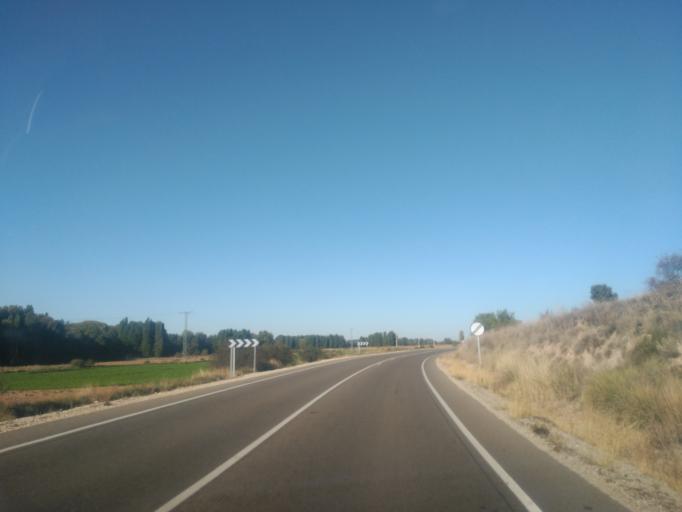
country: ES
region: Castille and Leon
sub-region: Provincia de Burgos
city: Penaranda de Duero
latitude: 41.6853
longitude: -3.4929
